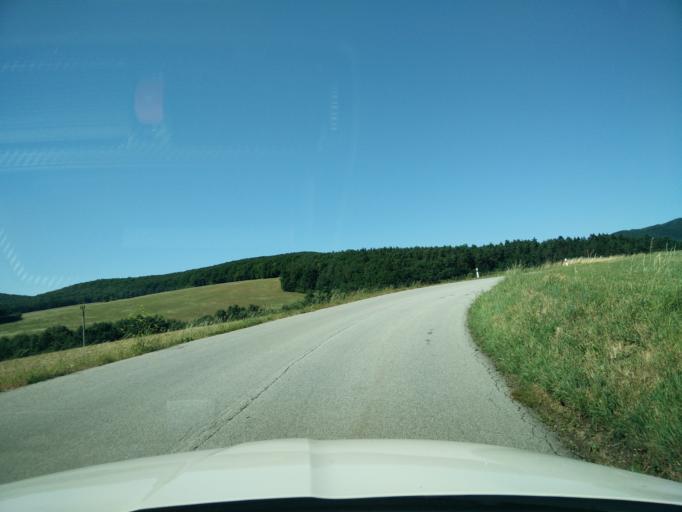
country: SK
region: Nitriansky
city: Prievidza
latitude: 48.7821
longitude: 18.6955
